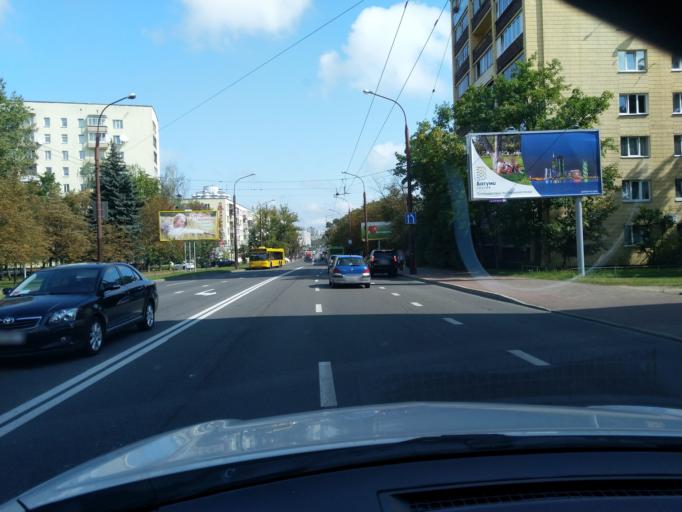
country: BY
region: Minsk
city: Minsk
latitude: 53.9164
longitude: 27.5721
